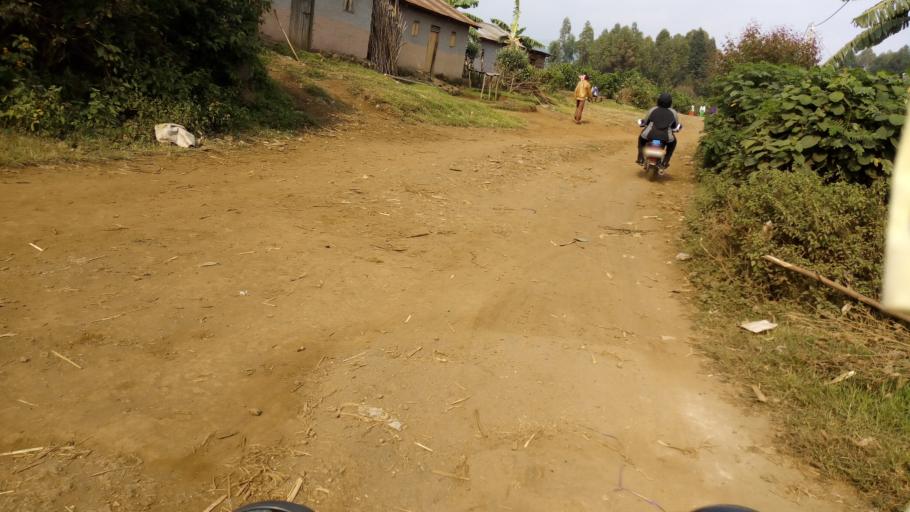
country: UG
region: Western Region
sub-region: Kisoro District
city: Kisoro
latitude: -1.3079
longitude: 29.6604
